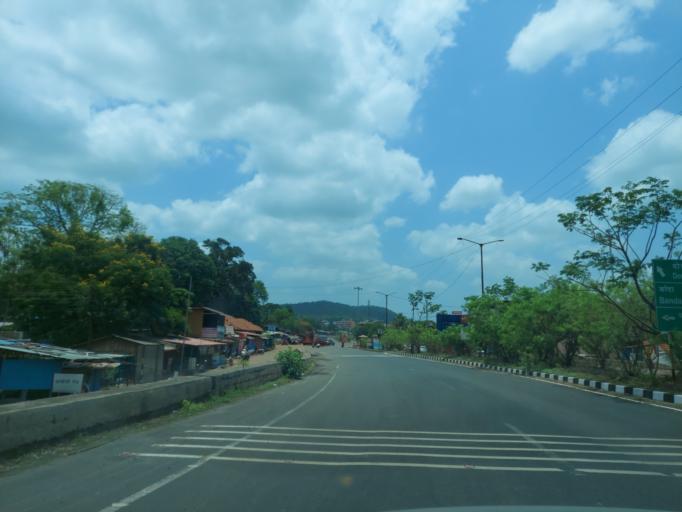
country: IN
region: Maharashtra
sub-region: Sindhudurg
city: Savantvadi
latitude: 15.8176
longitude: 73.8641
